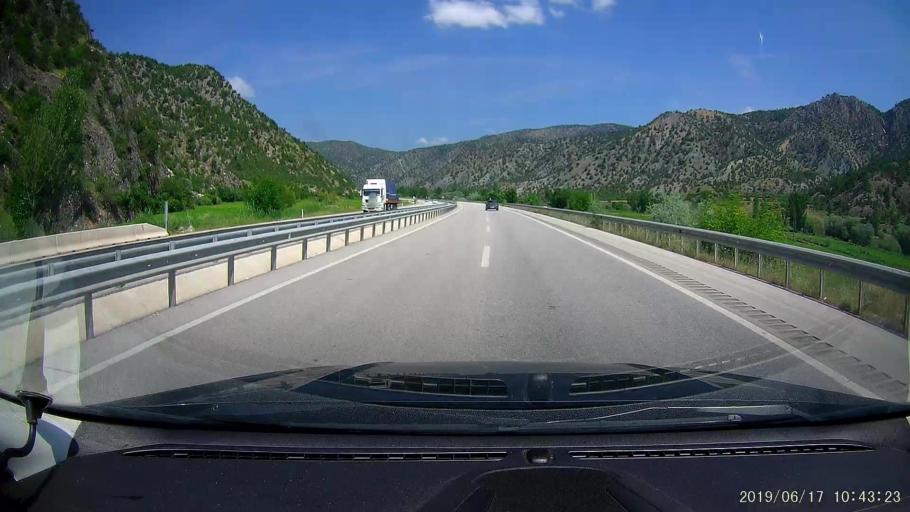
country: TR
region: Corum
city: Kargi
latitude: 41.0637
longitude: 34.5367
